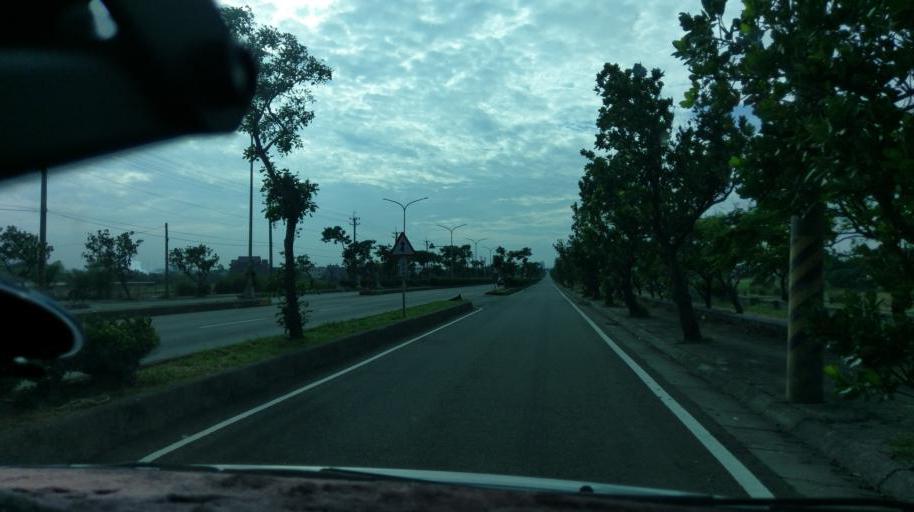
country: TW
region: Taiwan
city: Fengyuan
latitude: 24.2985
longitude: 120.5689
